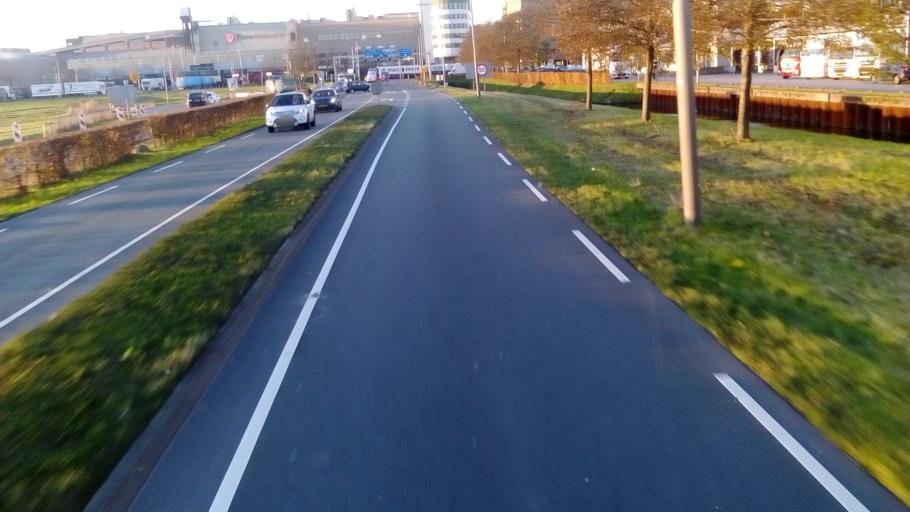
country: NL
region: South Holland
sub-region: Gemeente Westland
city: Honselersdijk
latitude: 51.9946
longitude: 4.2315
